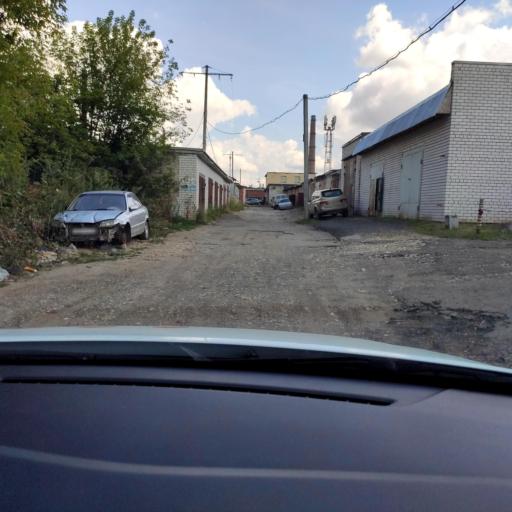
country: RU
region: Tatarstan
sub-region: Gorod Kazan'
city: Kazan
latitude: 55.7595
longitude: 49.1983
